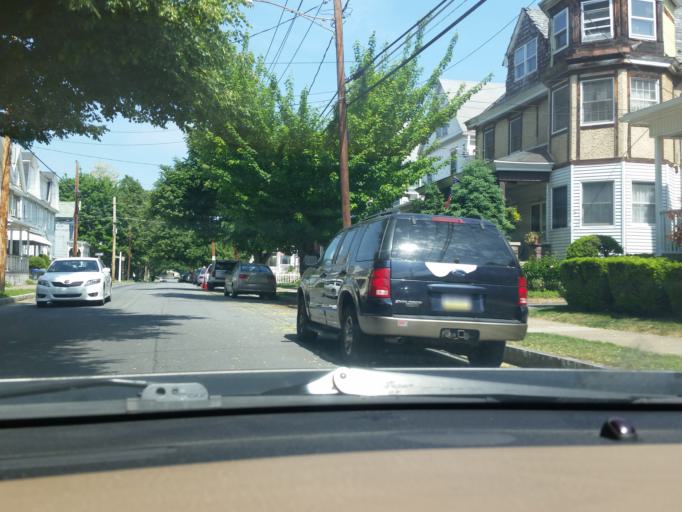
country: US
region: Pennsylvania
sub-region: Luzerne County
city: Wilkes-Barre
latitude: 41.2430
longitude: -75.8984
